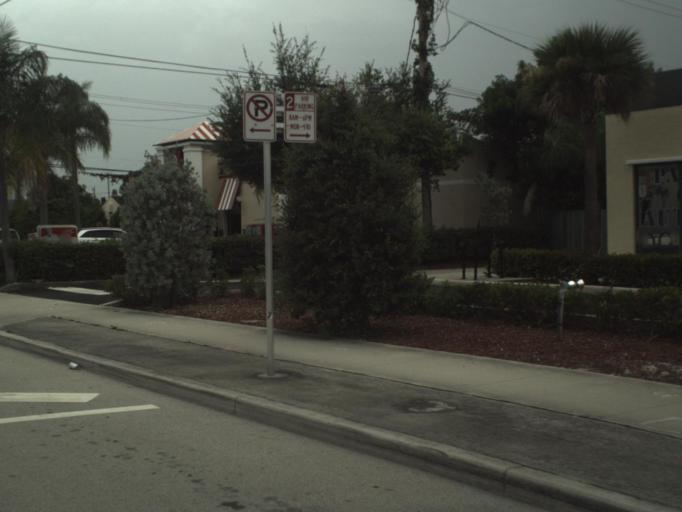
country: US
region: Florida
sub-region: Palm Beach County
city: Palm Beach
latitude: 26.6832
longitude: -80.0546
